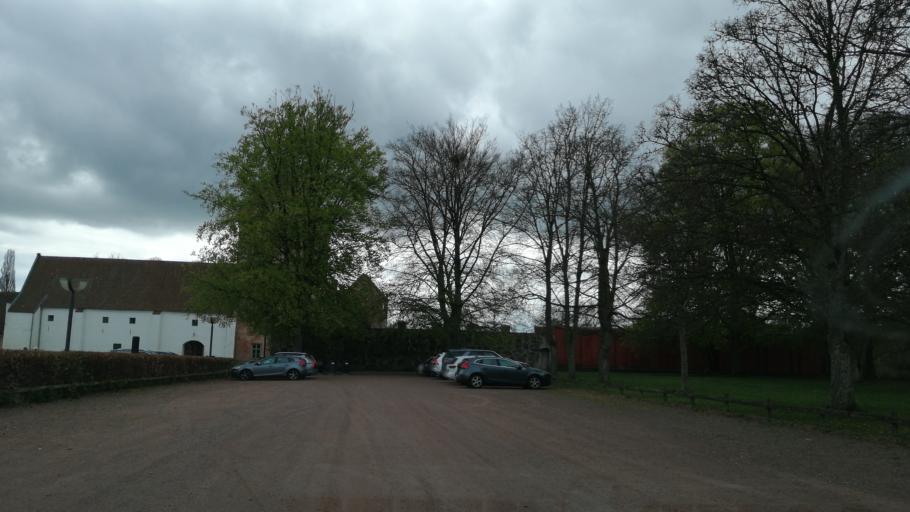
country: SE
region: Skane
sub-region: Kristianstads Kommun
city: Fjalkinge
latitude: 56.0865
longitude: 14.3485
